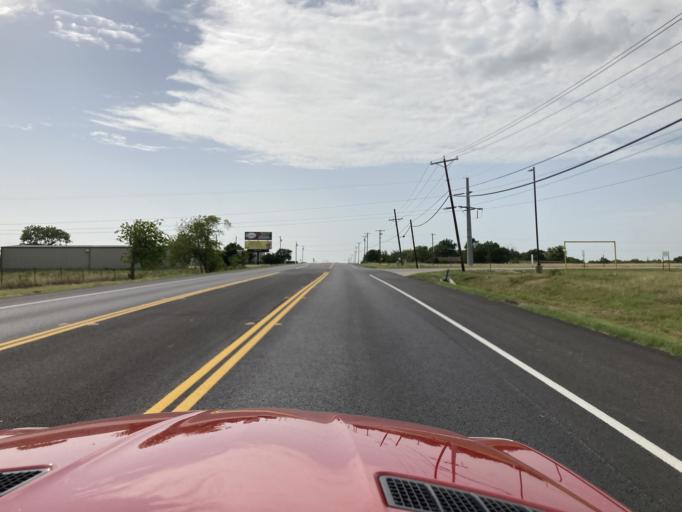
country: US
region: Texas
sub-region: Navarro County
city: Corsicana
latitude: 32.0616
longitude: -96.4340
